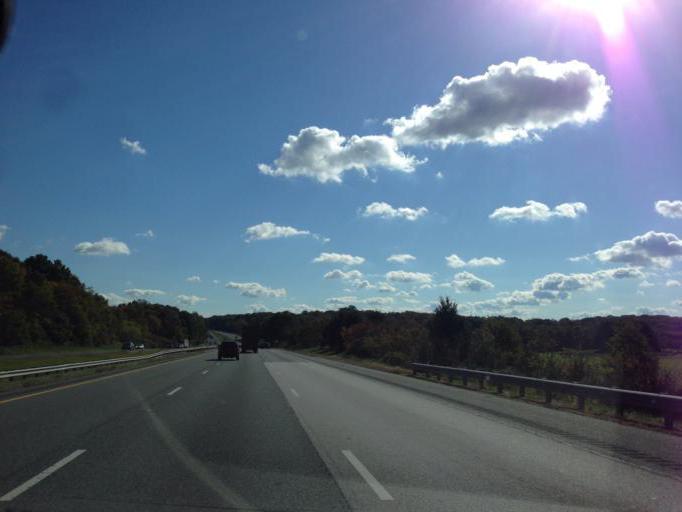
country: US
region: Maryland
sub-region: Carroll County
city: Mount Airy
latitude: 39.3398
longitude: -77.0618
